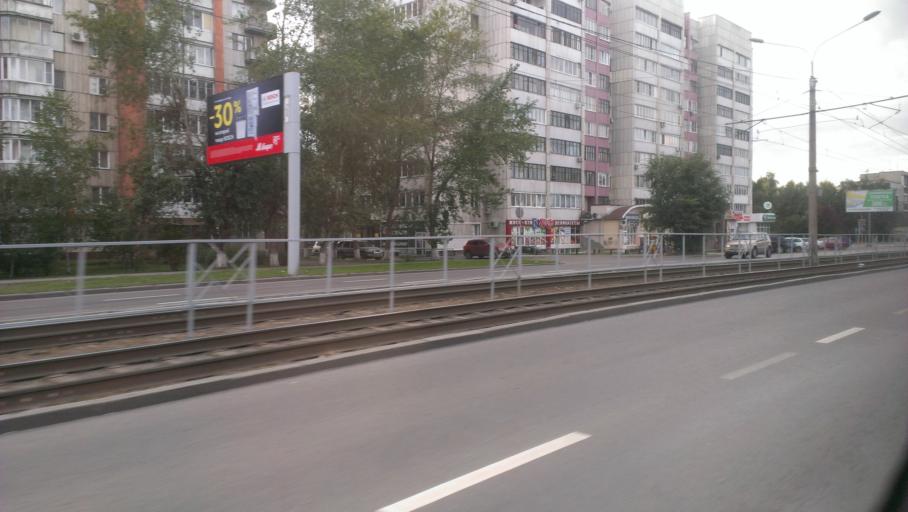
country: RU
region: Altai Krai
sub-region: Gorod Barnaulskiy
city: Barnaul
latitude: 53.3438
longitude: 83.7678
